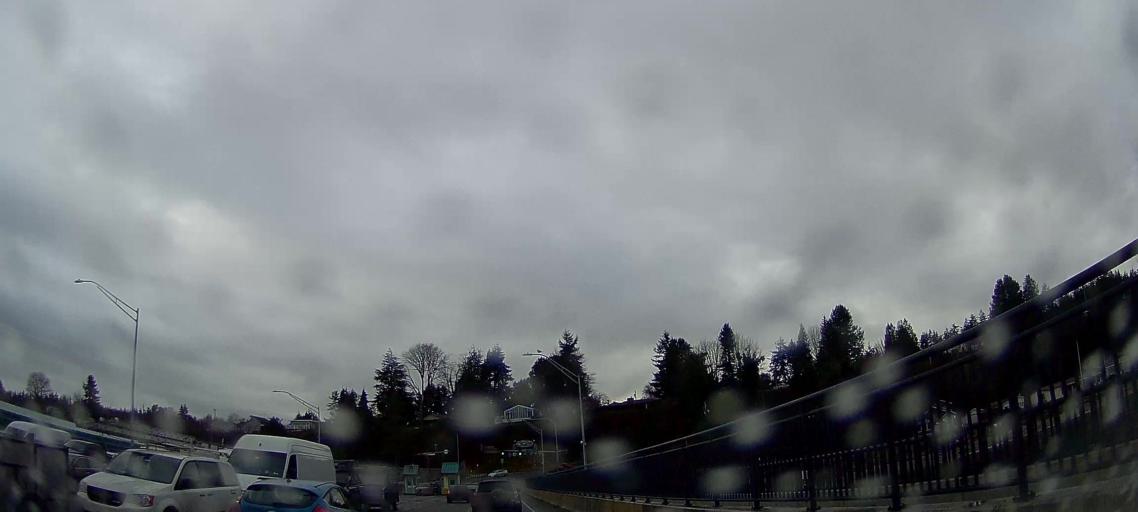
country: US
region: Washington
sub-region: Snohomish County
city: Mukilteo
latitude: 47.9756
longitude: -122.3494
